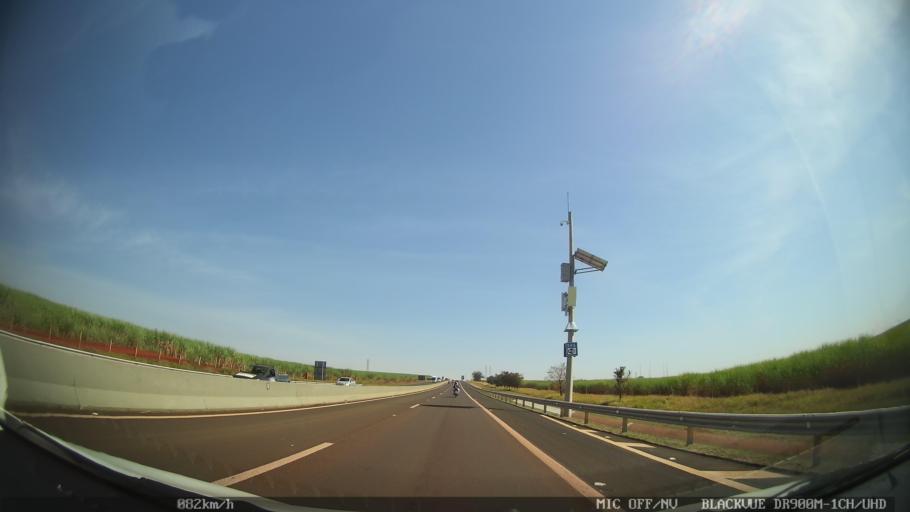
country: BR
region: Sao Paulo
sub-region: Ribeirao Preto
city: Ribeirao Preto
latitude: -21.1659
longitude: -47.8819
